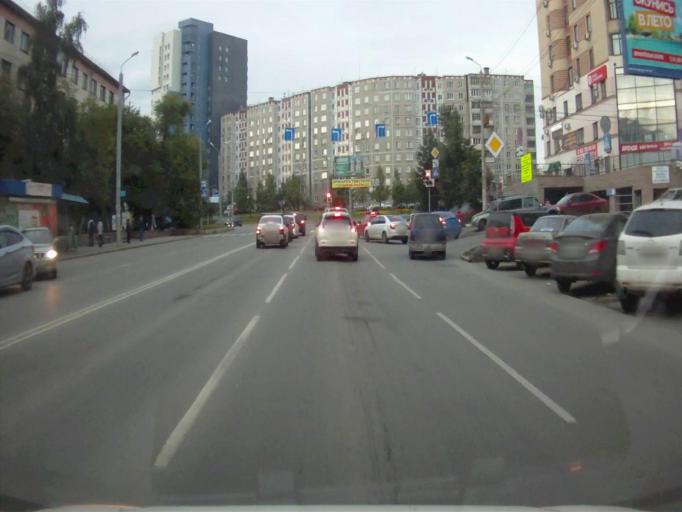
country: RU
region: Chelyabinsk
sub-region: Gorod Chelyabinsk
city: Chelyabinsk
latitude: 55.1540
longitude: 61.3816
